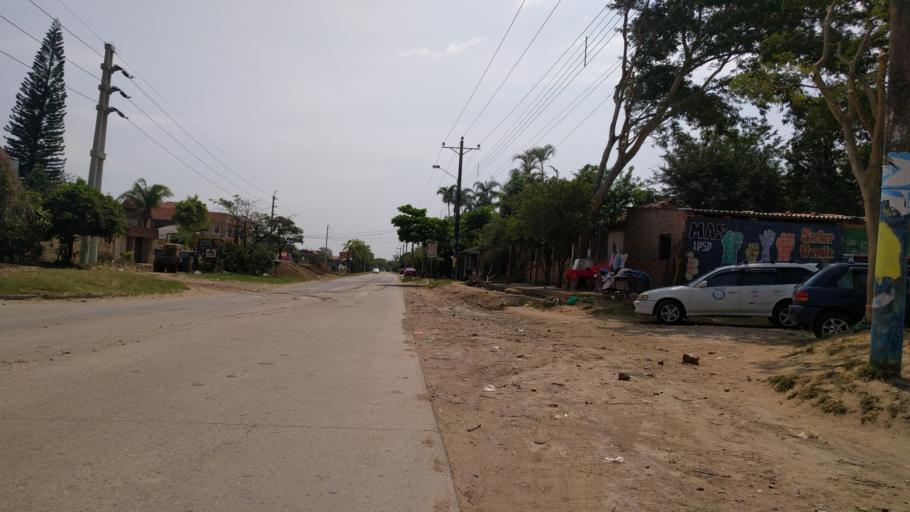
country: BO
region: Santa Cruz
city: Santa Cruz de la Sierra
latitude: -17.8264
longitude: -63.2141
